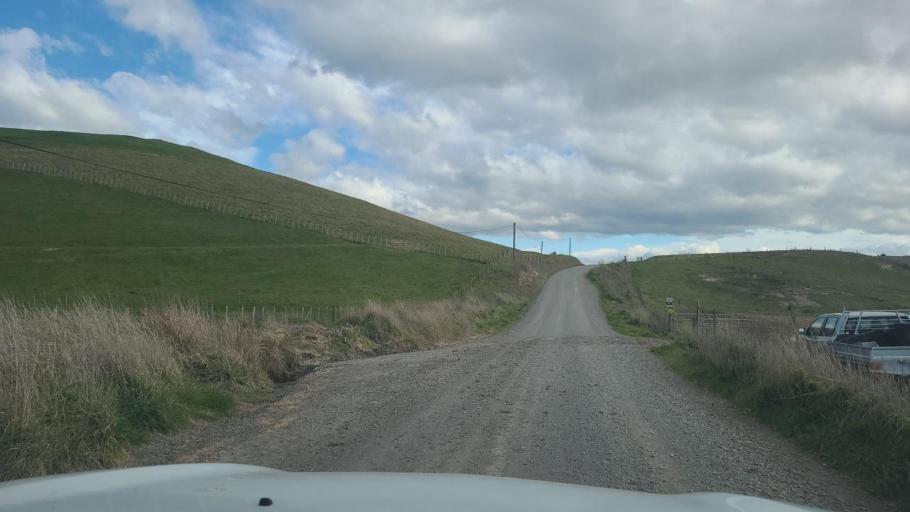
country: NZ
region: Hawke's Bay
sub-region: Hastings District
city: Hastings
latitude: -39.6625
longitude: 176.6640
